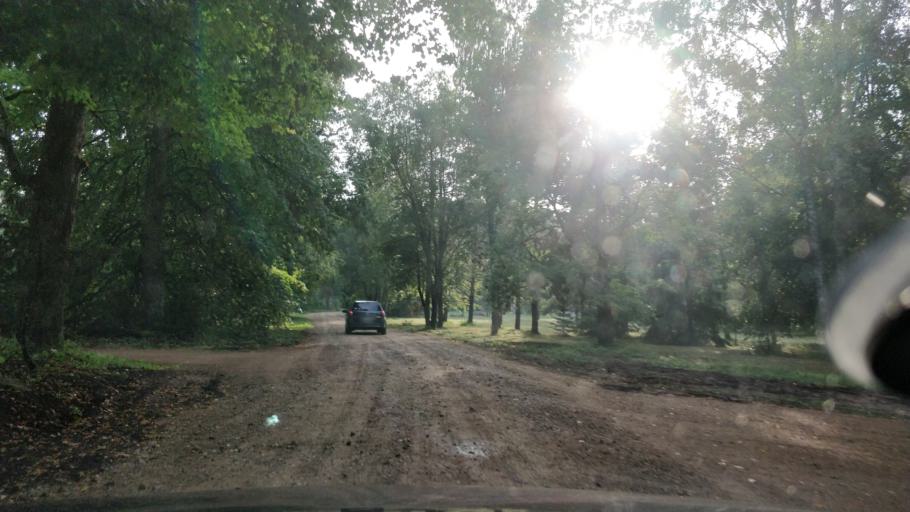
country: LV
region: Sigulda
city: Sigulda
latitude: 57.0999
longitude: 24.8036
